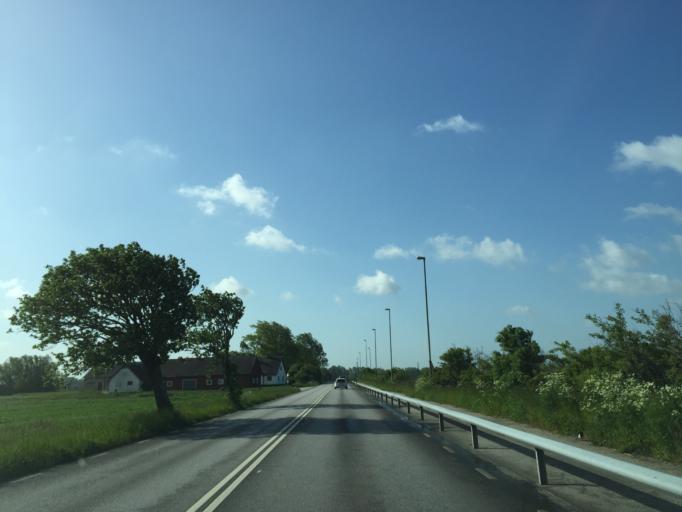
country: SE
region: Skane
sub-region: Burlovs Kommun
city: Arloev
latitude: 55.6499
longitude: 13.0565
